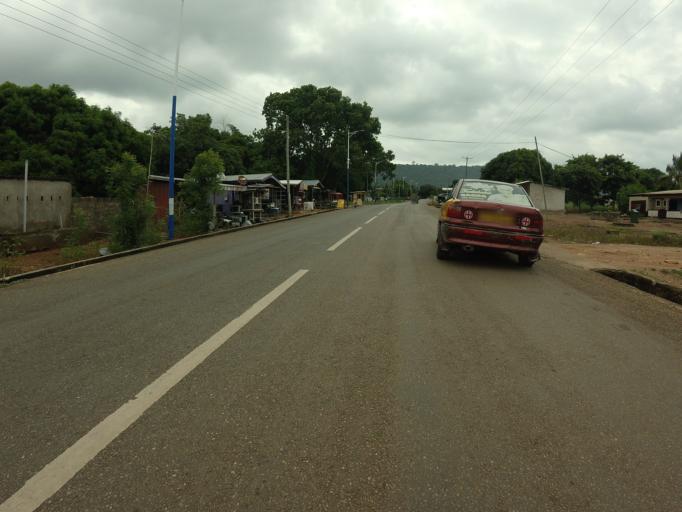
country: GH
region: Volta
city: Ho
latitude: 6.6306
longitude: 0.4870
